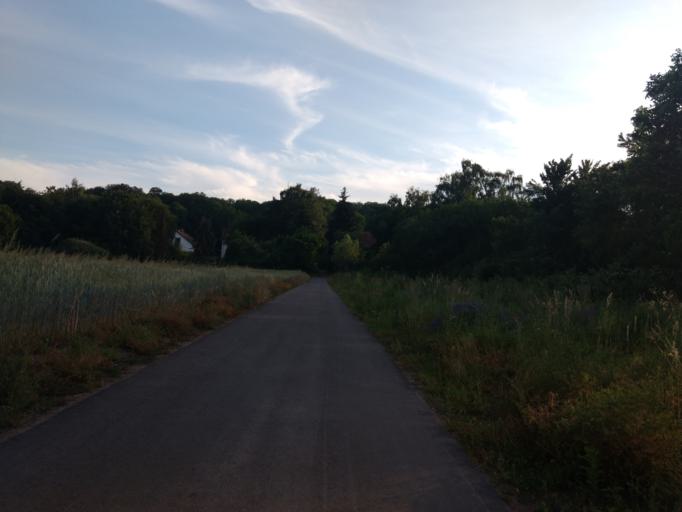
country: DE
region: Saarland
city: Saarlouis
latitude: 49.3100
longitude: 6.7269
